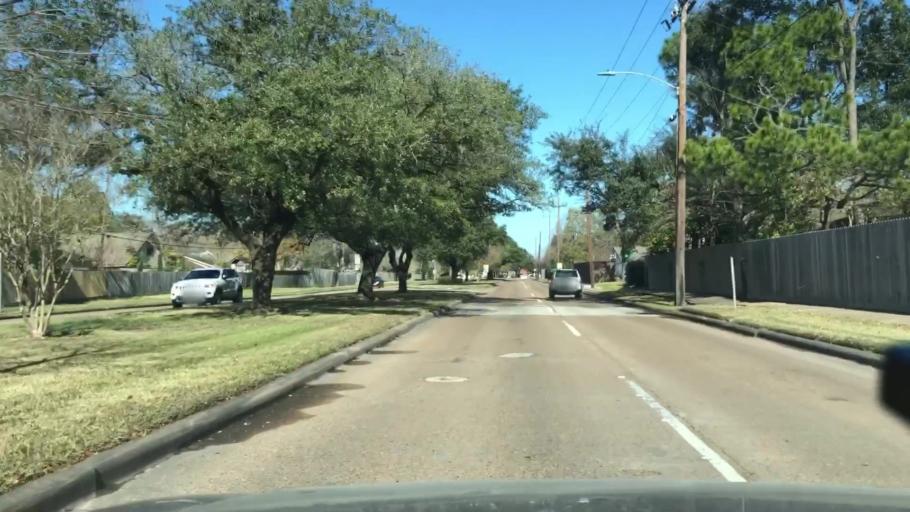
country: US
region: Texas
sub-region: Harris County
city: Bellaire
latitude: 29.6820
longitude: -95.4927
